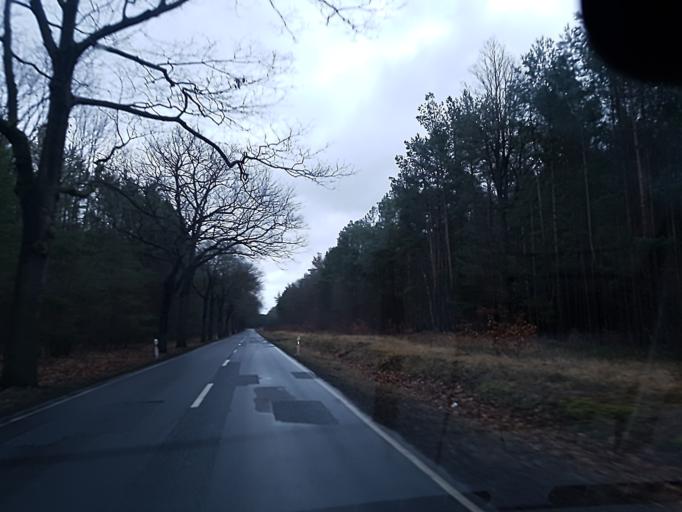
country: DE
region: Brandenburg
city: Hohenleipisch
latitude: 51.5284
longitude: 13.5846
